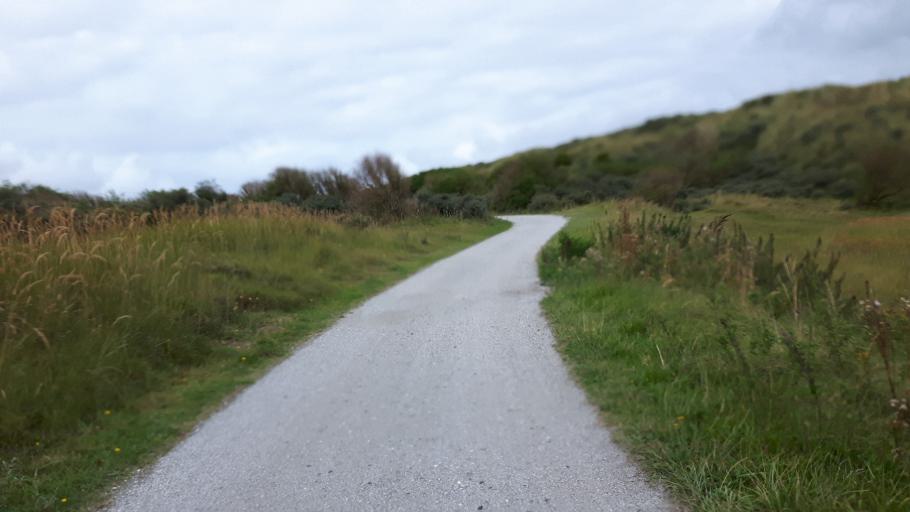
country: NL
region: Friesland
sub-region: Gemeente Ameland
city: Nes
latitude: 53.4575
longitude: 5.7239
